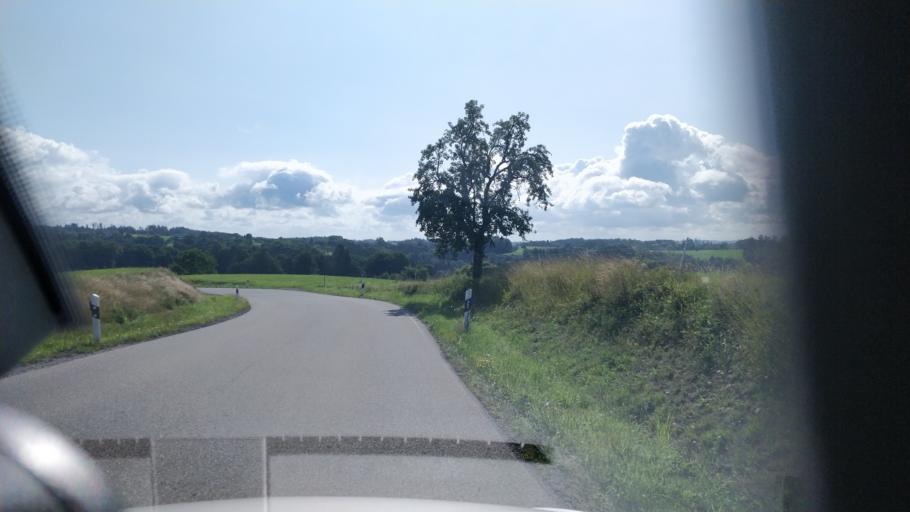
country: DE
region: Baden-Wuerttemberg
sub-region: Regierungsbezirk Stuttgart
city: Murrhardt
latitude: 49.0142
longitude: 9.5918
